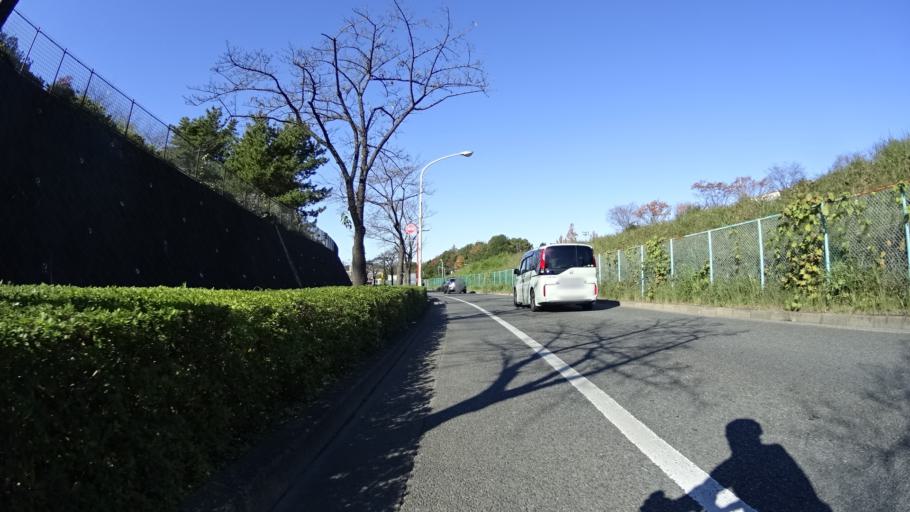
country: JP
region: Tokyo
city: Hino
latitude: 35.6121
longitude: 139.4172
